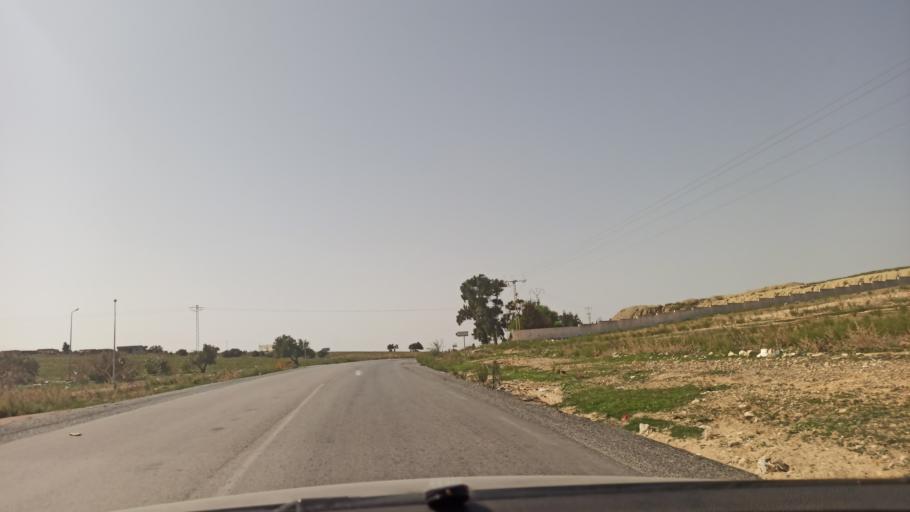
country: TN
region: Manouba
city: Manouba
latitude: 36.7379
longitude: 10.0841
